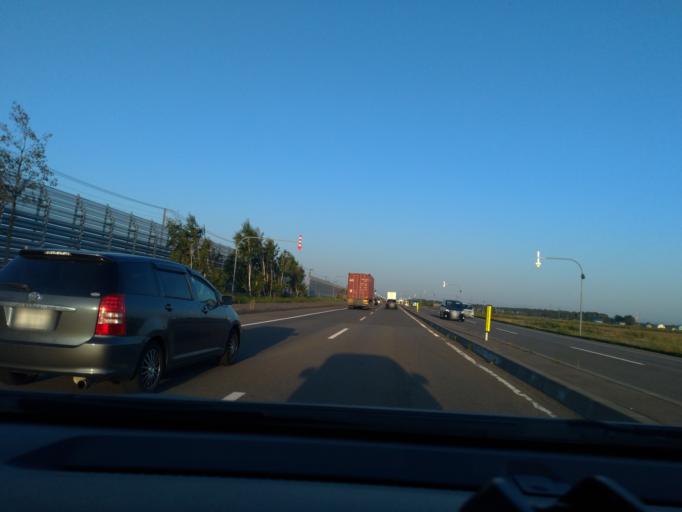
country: JP
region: Hokkaido
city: Tobetsu
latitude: 43.1795
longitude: 141.4661
